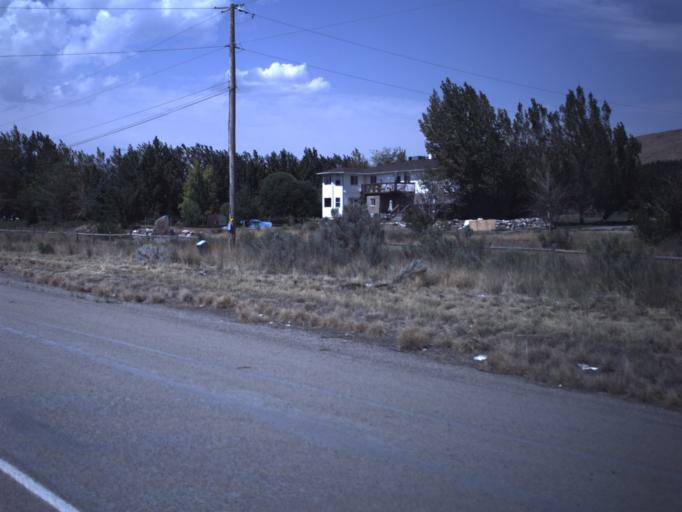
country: US
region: Utah
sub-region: Utah County
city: Eagle Mountain
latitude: 40.3804
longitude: -111.9820
